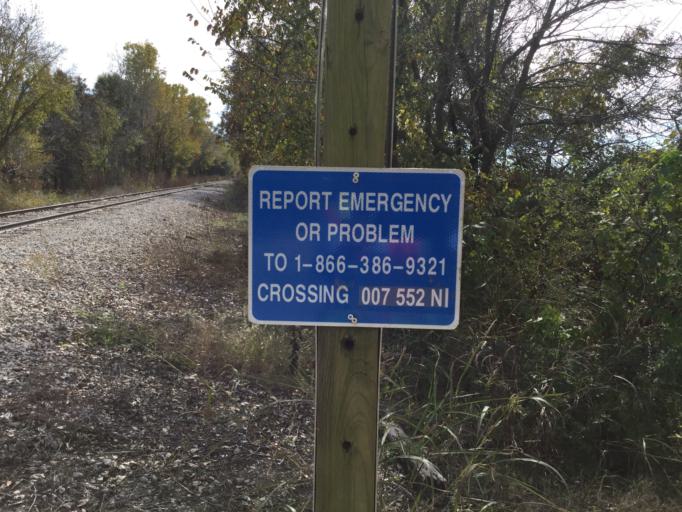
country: US
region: Kansas
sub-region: Montgomery County
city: Coffeyville
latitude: 37.1229
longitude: -95.5989
